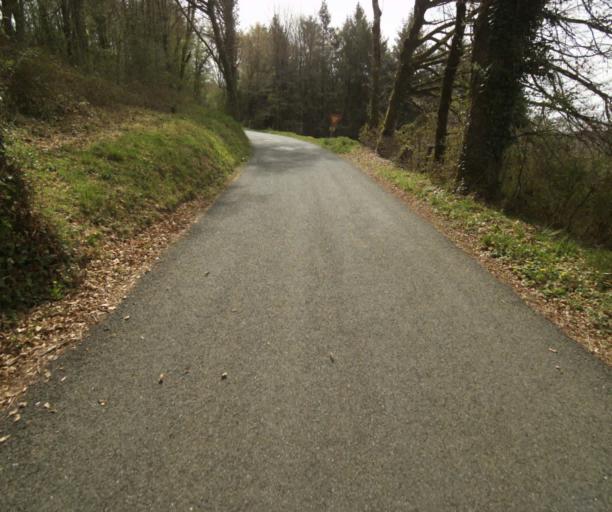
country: FR
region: Limousin
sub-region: Departement de la Correze
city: Naves
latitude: 45.2967
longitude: 1.7753
